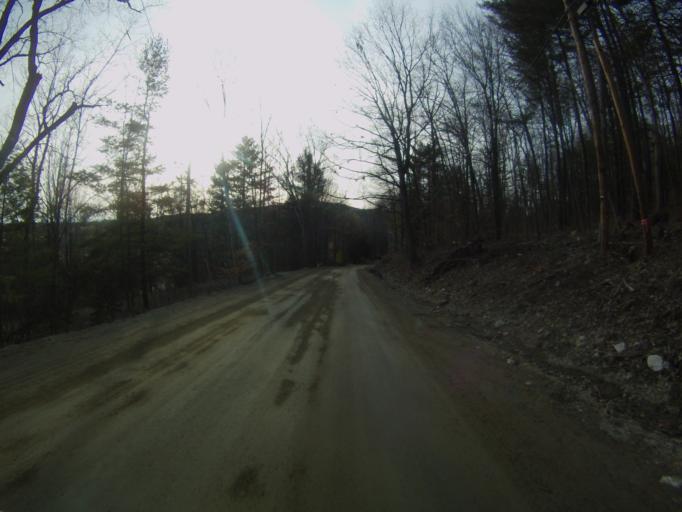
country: US
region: Vermont
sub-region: Addison County
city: Middlebury (village)
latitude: 44.0317
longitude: -73.2652
